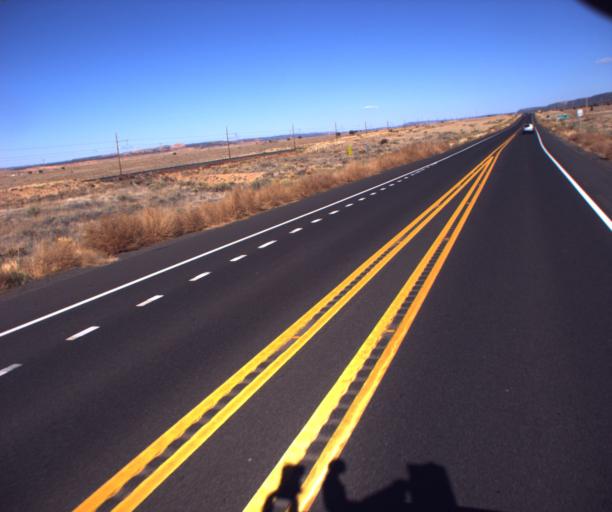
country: US
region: Arizona
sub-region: Coconino County
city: Kaibito
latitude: 36.4618
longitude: -110.6906
